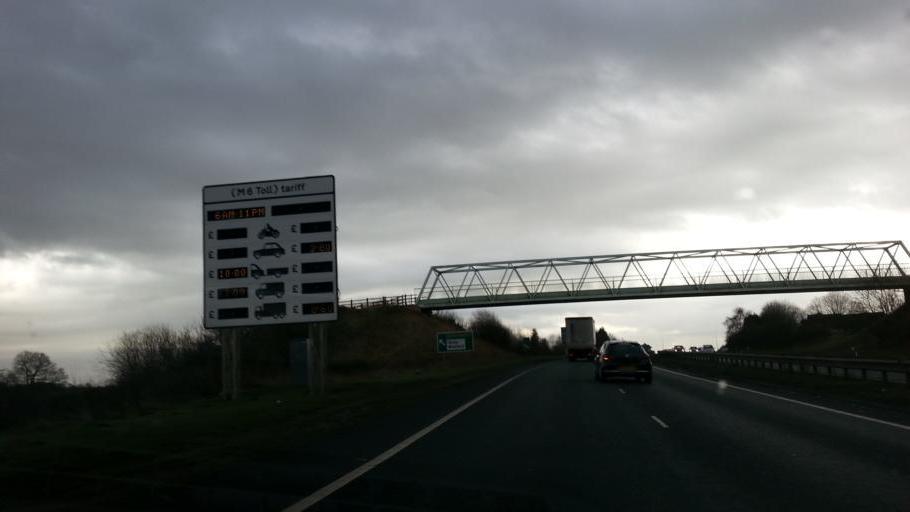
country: GB
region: England
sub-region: Staffordshire
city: Shenstone
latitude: 52.6461
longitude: -1.8062
